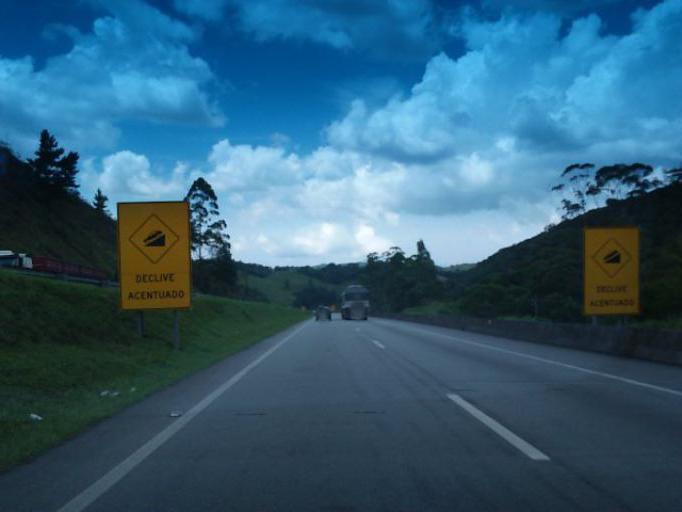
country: BR
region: Sao Paulo
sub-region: Juquitiba
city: Juquitiba
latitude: -23.9965
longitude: -47.1486
